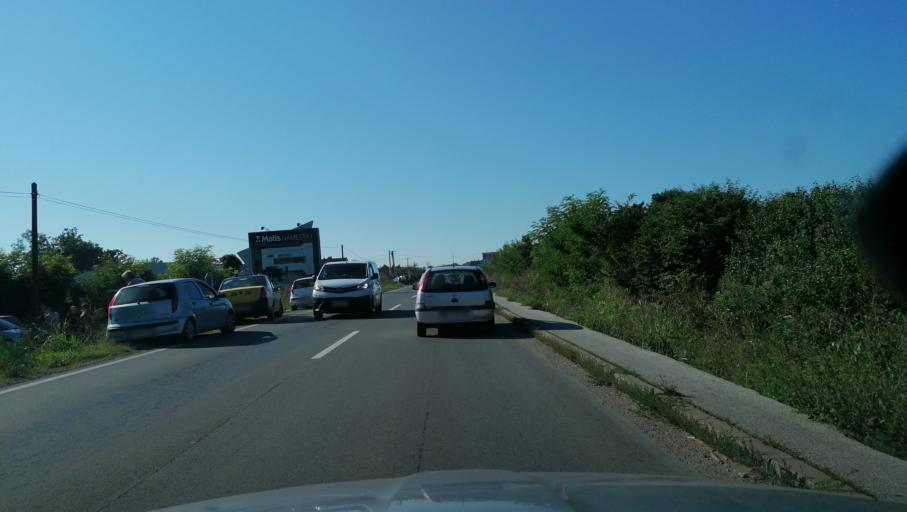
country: RS
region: Central Serbia
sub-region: Raski Okrug
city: Kraljevo
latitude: 43.7588
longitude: 20.6518
